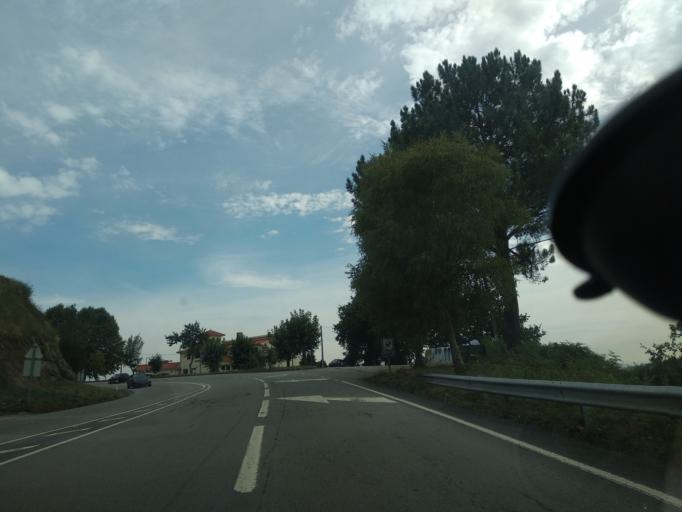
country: PT
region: Braga
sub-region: Povoa de Lanhoso
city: Povoa de Lanhoso
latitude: 41.6125
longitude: -8.2498
